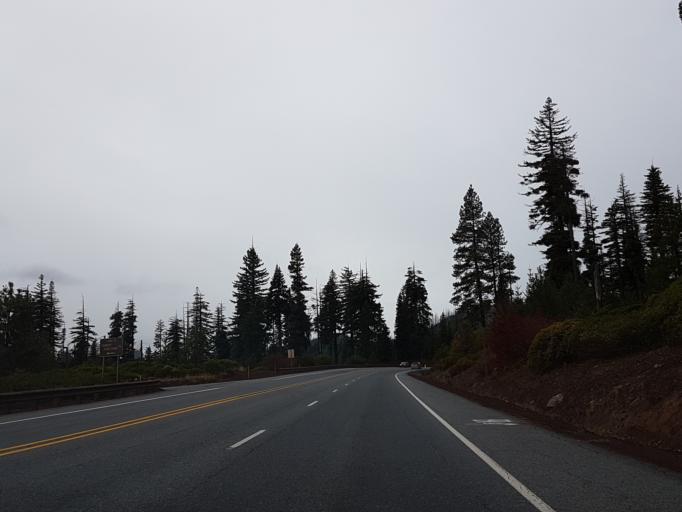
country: US
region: Oregon
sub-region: Deschutes County
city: Sisters
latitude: 44.4205
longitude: -121.7884
